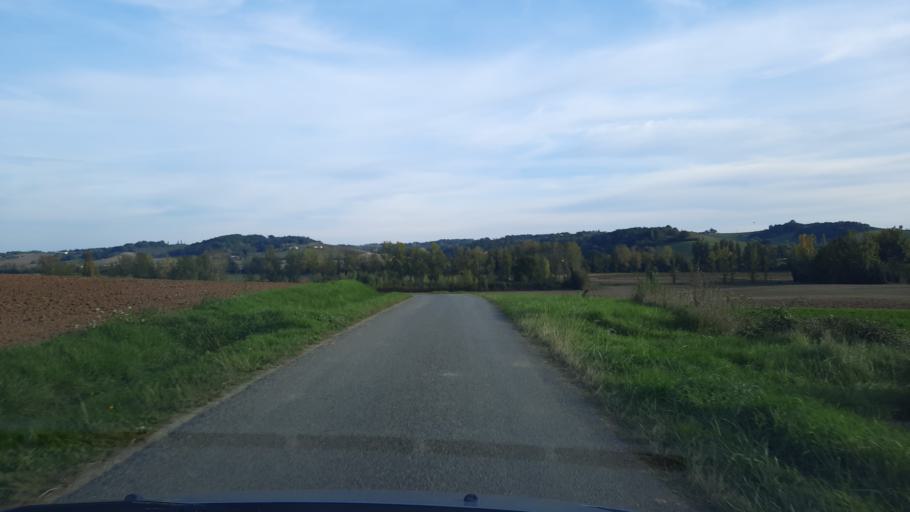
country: FR
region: Midi-Pyrenees
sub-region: Departement du Tarn-et-Garonne
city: Lafrancaise
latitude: 44.1695
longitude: 1.2787
